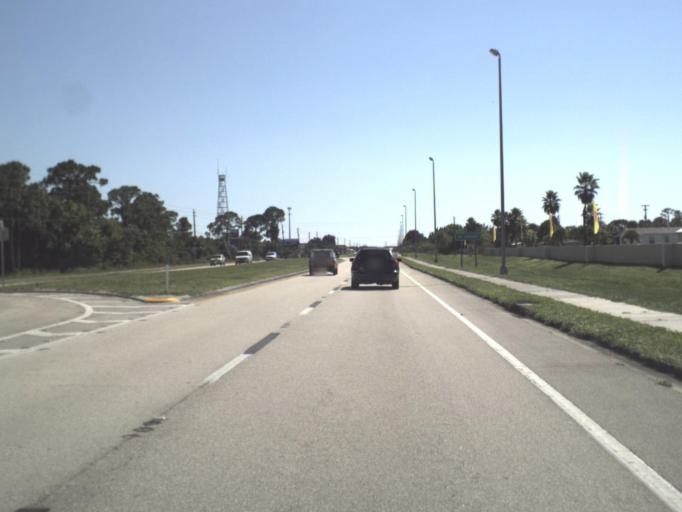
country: US
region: Florida
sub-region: Sarasota County
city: North Port
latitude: 26.9757
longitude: -82.2087
